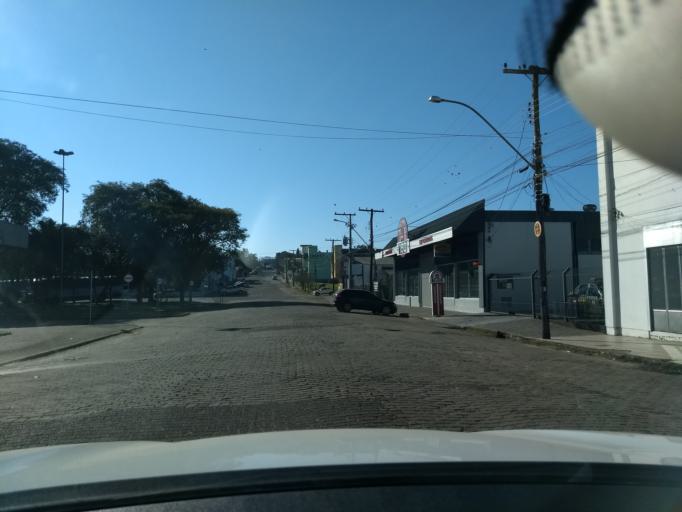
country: BR
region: Rio Grande do Sul
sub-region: Santa Cruz Do Sul
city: Santa Cruz do Sul
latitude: -29.7195
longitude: -52.4450
